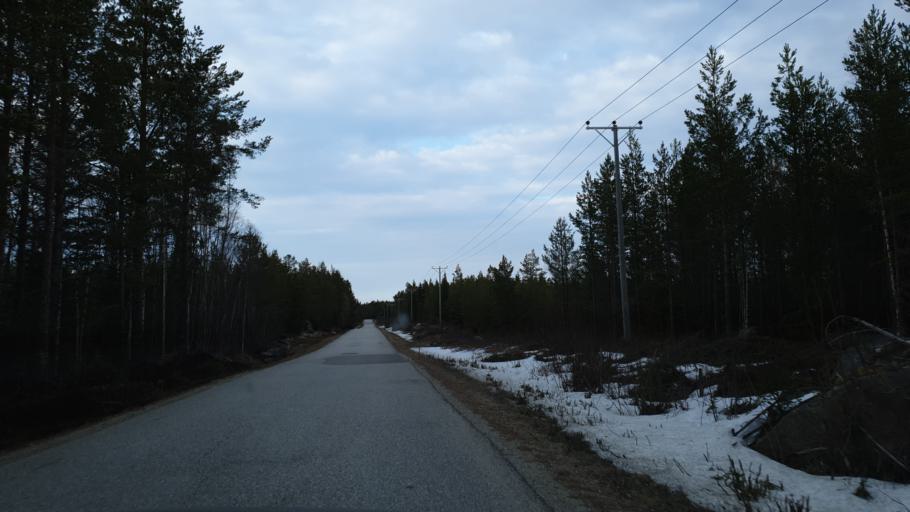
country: SE
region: Vaesternorrland
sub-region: Sundsvalls Kommun
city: Njurundabommen
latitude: 61.9922
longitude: 17.3806
